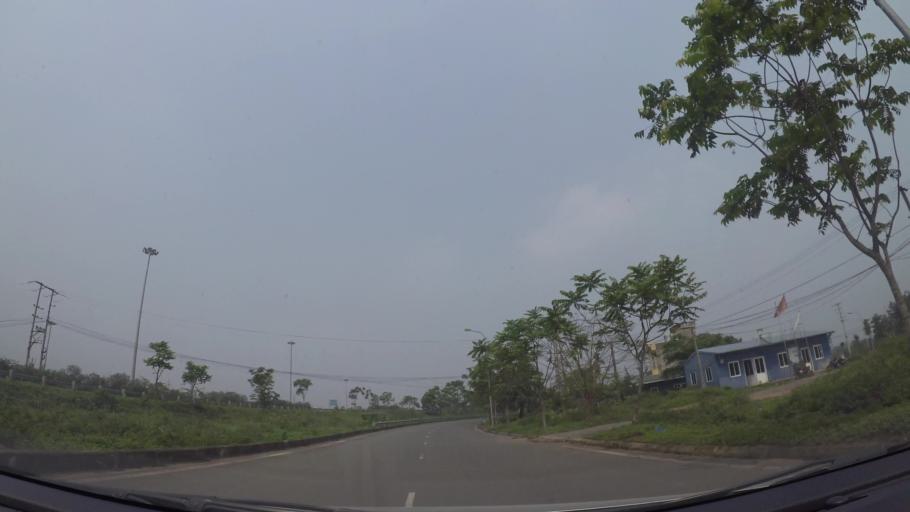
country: VN
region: Ha Noi
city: Lien Quan
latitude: 20.9908
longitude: 105.5293
